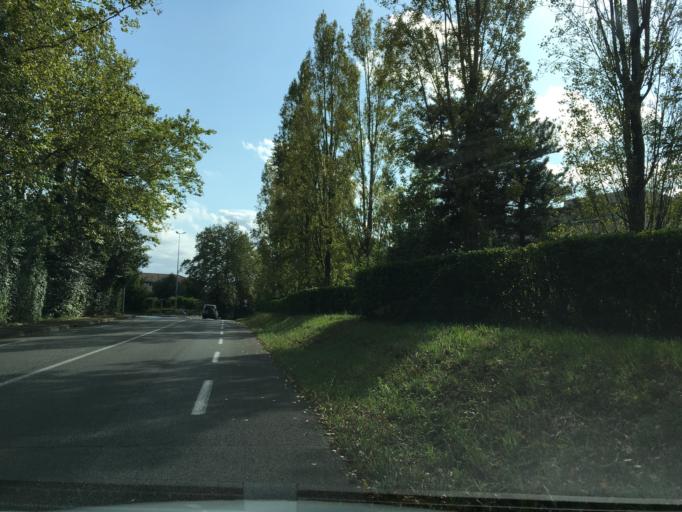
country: FR
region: Aquitaine
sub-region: Departement des Pyrenees-Atlantiques
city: Bayonne
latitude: 43.4733
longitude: -1.4859
